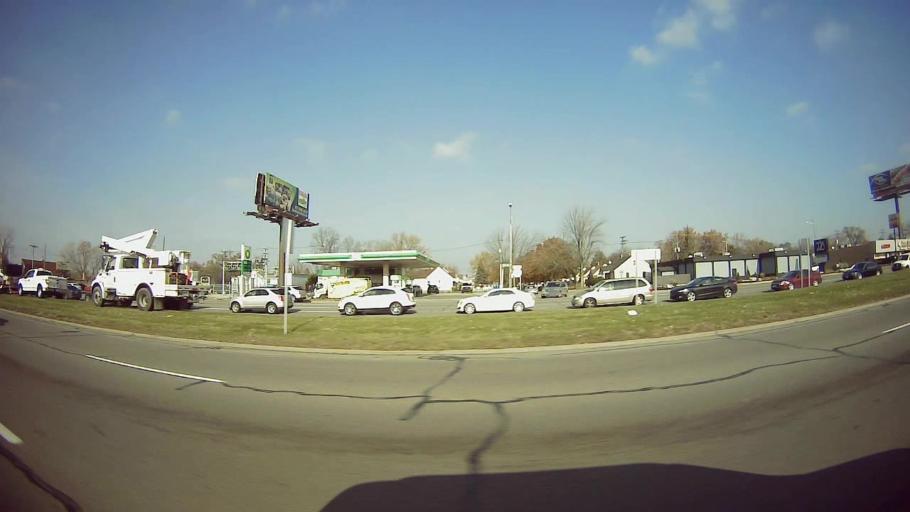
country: US
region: Michigan
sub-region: Wayne County
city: Dearborn
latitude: 42.3287
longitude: -83.2241
